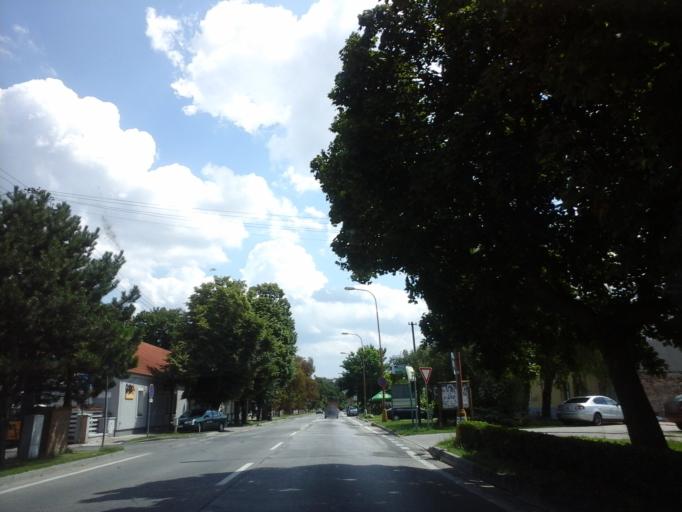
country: AT
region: Burgenland
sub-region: Politischer Bezirk Neusiedl am See
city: Deutsch Jahrndorf
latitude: 48.0530
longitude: 17.1483
